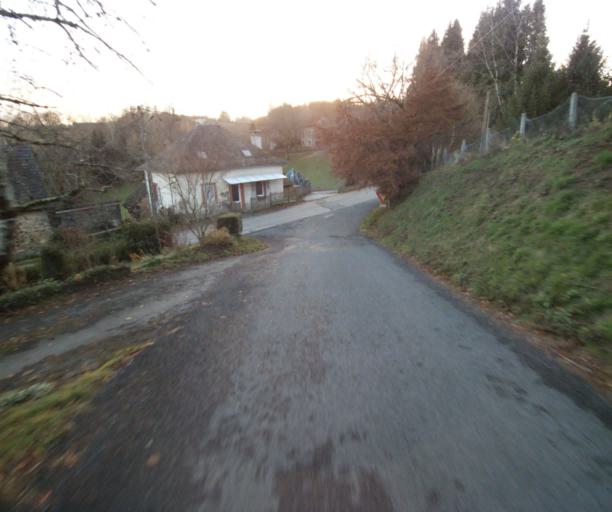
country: FR
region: Limousin
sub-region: Departement de la Correze
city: Laguenne
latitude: 45.2358
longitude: 1.7698
